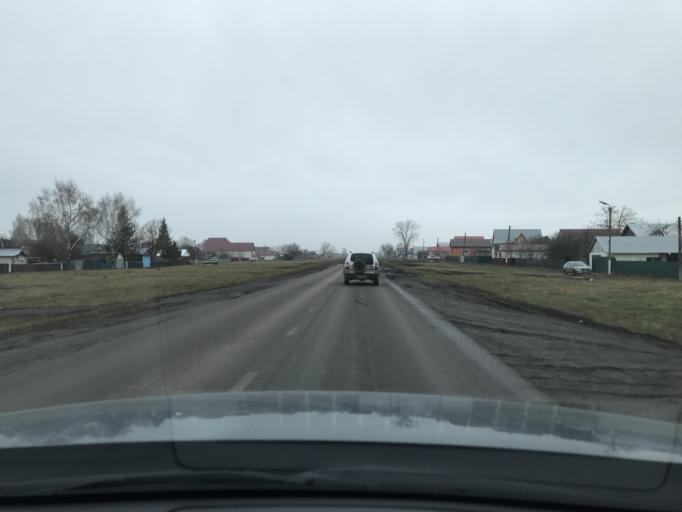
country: RU
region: Penza
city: Zemetchino
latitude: 53.5087
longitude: 42.6380
